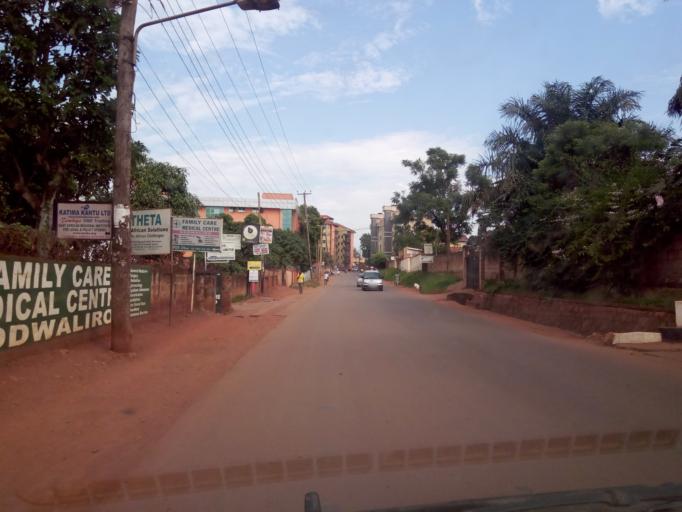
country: UG
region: Central Region
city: Kampala Central Division
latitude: 0.3413
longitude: 32.5840
